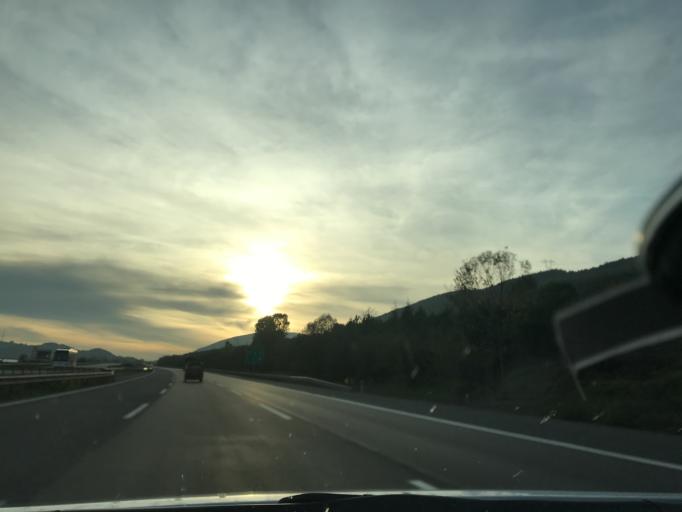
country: TR
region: Duzce
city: Gumusova
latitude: 40.8369
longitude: 30.9441
